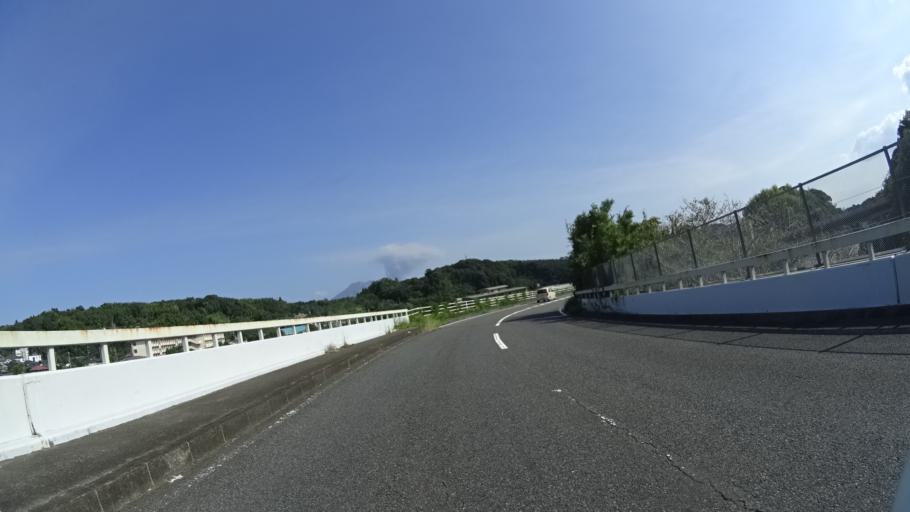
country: JP
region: Kagoshima
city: Kagoshima-shi
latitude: 31.6532
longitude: 130.5519
